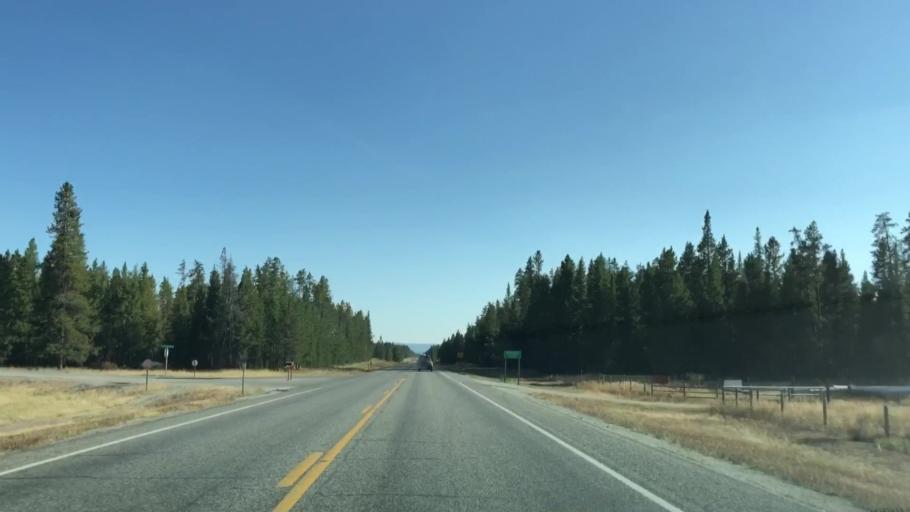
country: US
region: Montana
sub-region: Gallatin County
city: West Yellowstone
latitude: 44.7777
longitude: -111.1133
